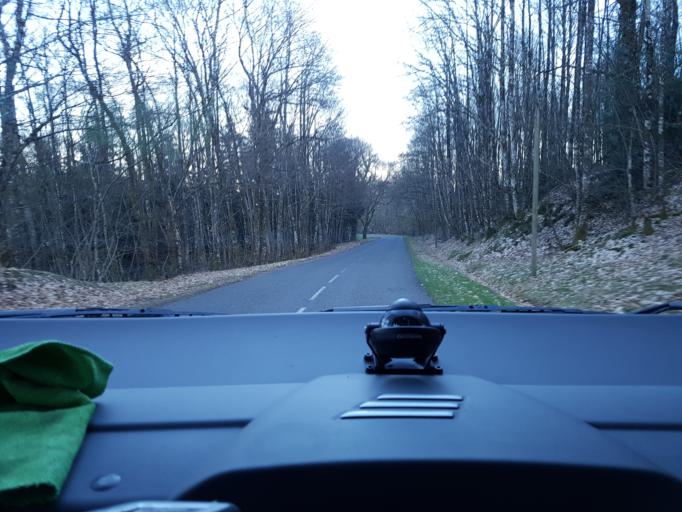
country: FR
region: Bourgogne
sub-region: Departement de Saone-et-Loire
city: Etang-sur-Arroux
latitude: 46.9202
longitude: 4.0714
